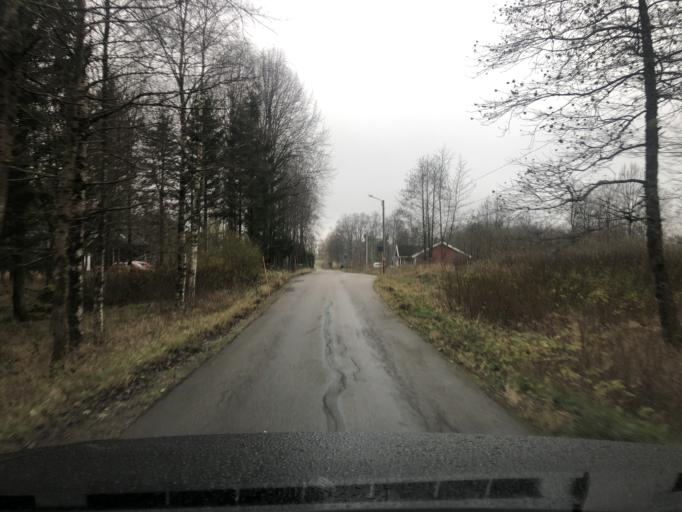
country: SE
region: Vaestra Goetaland
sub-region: Boras Kommun
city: Sjomarken
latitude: 57.7641
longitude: 12.8481
